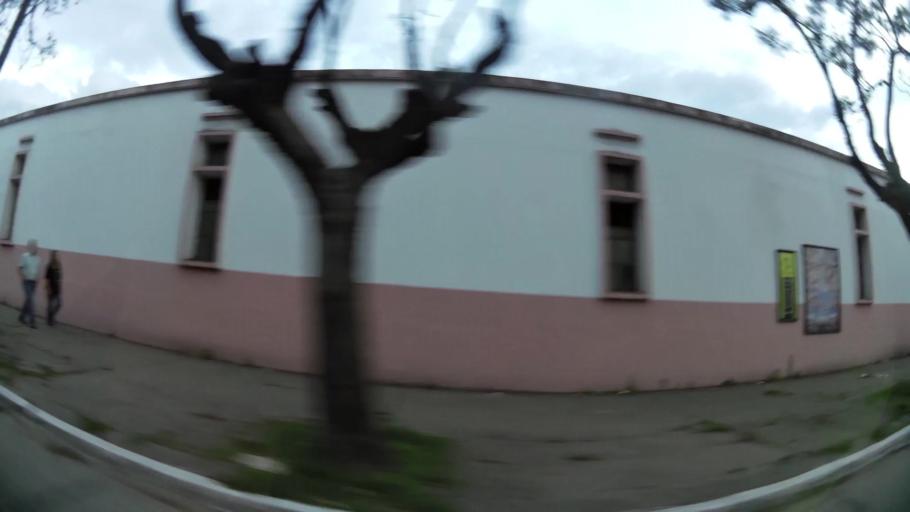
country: AR
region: Buenos Aires
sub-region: Partido de Quilmes
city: Quilmes
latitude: -34.7439
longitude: -58.2289
